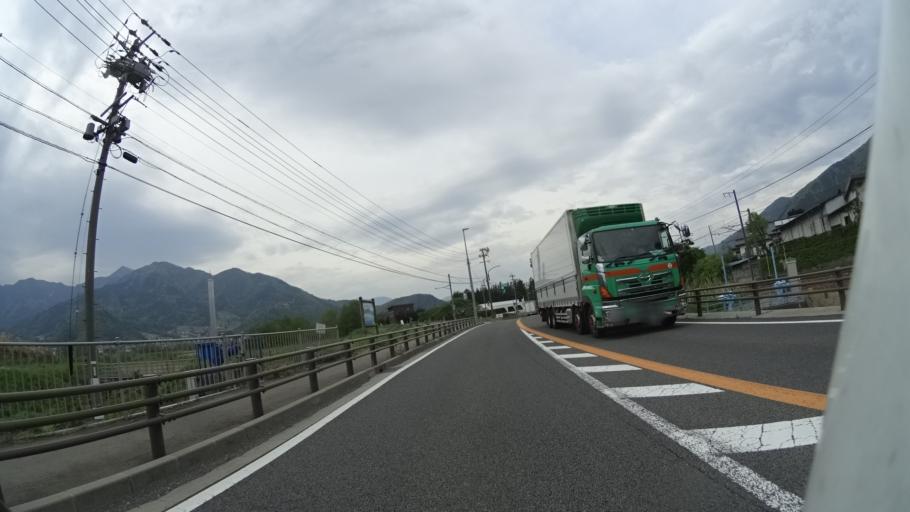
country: JP
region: Nagano
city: Ueda
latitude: 36.4740
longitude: 138.1604
